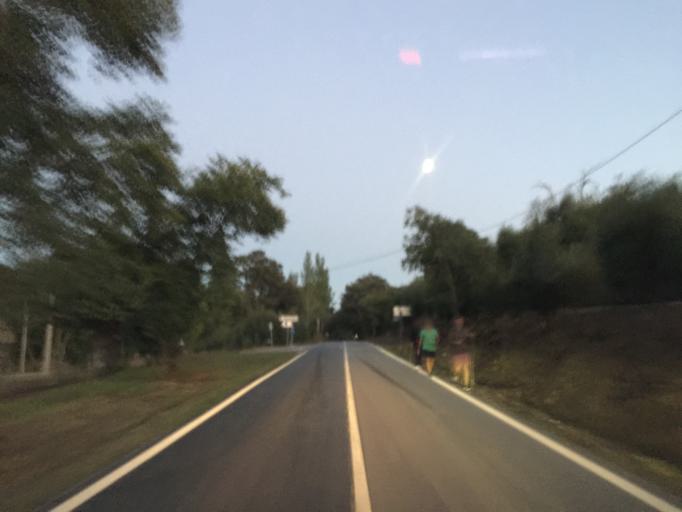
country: PT
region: Portalegre
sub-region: Castelo de Vide
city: Castelo de Vide
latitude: 39.3994
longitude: -7.4287
